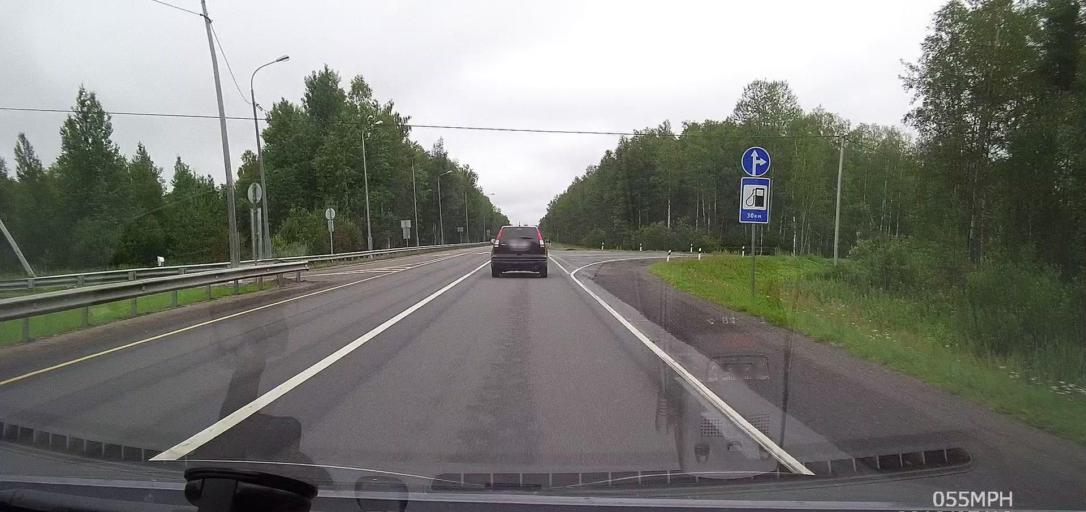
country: RU
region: Leningrad
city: Syas'stroy
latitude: 60.1984
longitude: 32.6649
